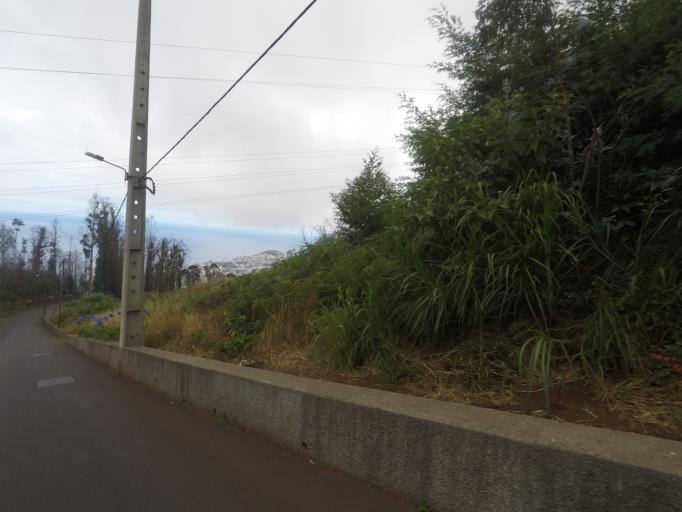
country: PT
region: Madeira
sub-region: Funchal
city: Nossa Senhora do Monte
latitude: 32.6693
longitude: -16.8834
